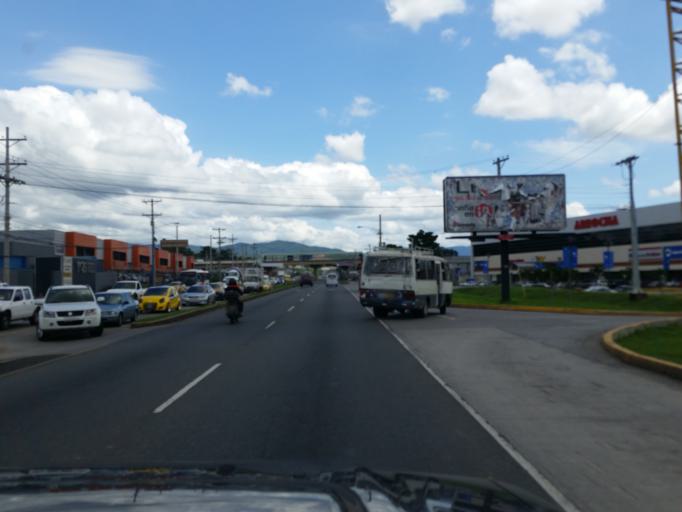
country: PA
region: Panama
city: Tocumen
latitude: 9.0779
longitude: -79.4007
